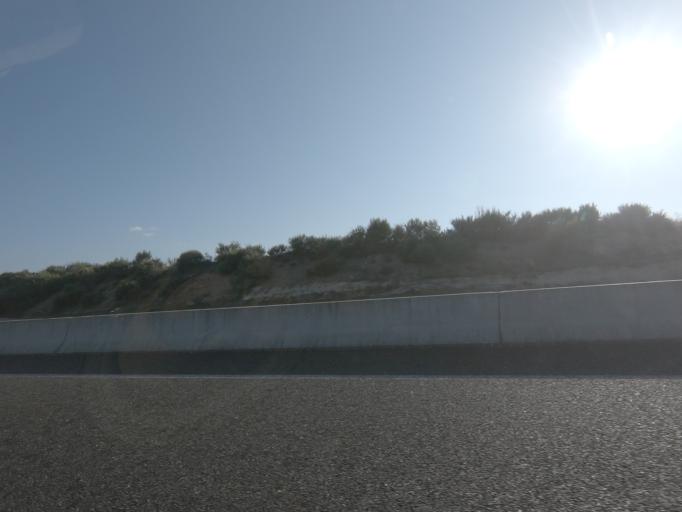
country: ES
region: Galicia
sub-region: Provincia de Ourense
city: Oimbra
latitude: 41.8239
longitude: -7.4197
